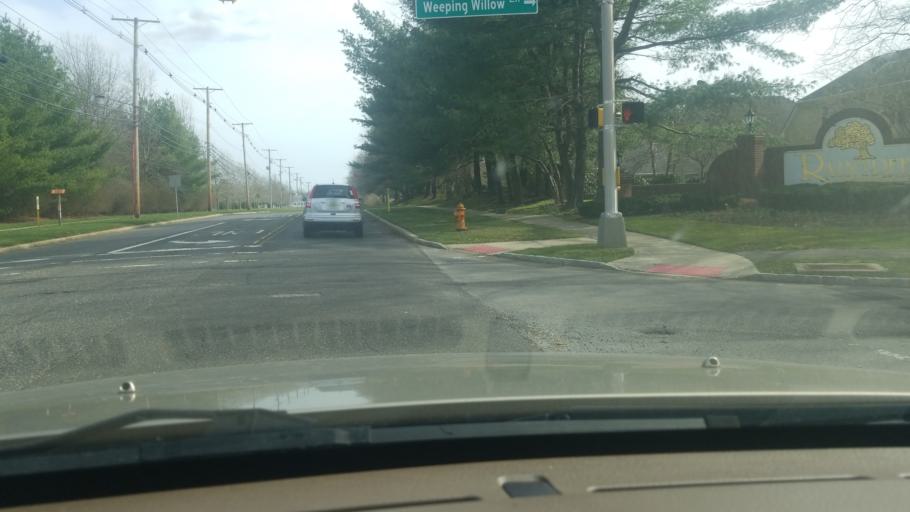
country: US
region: New Jersey
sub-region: Monmouth County
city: West Freehold
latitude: 40.2461
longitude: -74.3060
